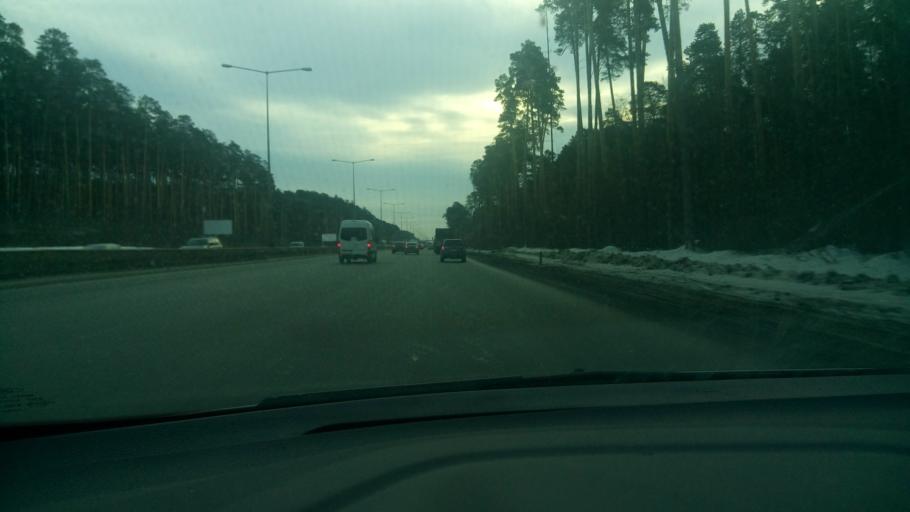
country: RU
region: Sverdlovsk
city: Yekaterinburg
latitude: 56.7933
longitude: 60.6591
